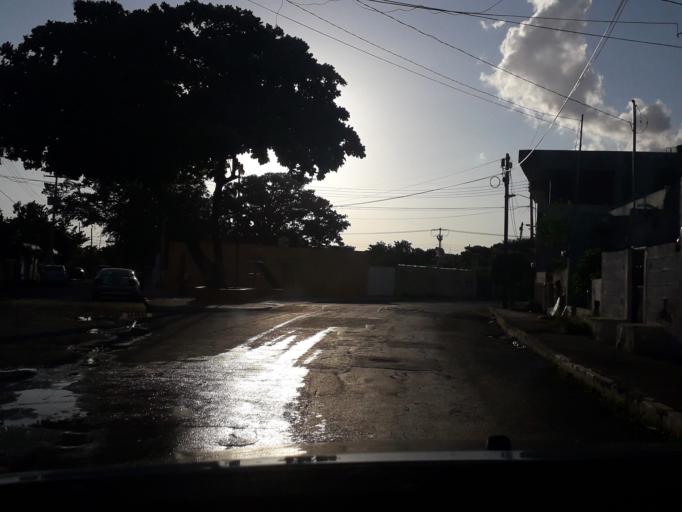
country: MX
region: Yucatan
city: Merida
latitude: 20.9628
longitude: -89.6425
